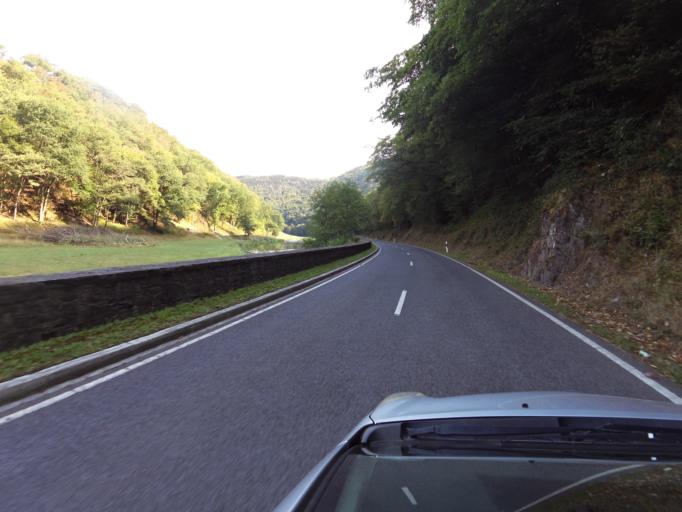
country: LU
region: Diekirch
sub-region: Canton de Diekirch
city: Bourscheid
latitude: 49.9225
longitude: 6.0730
